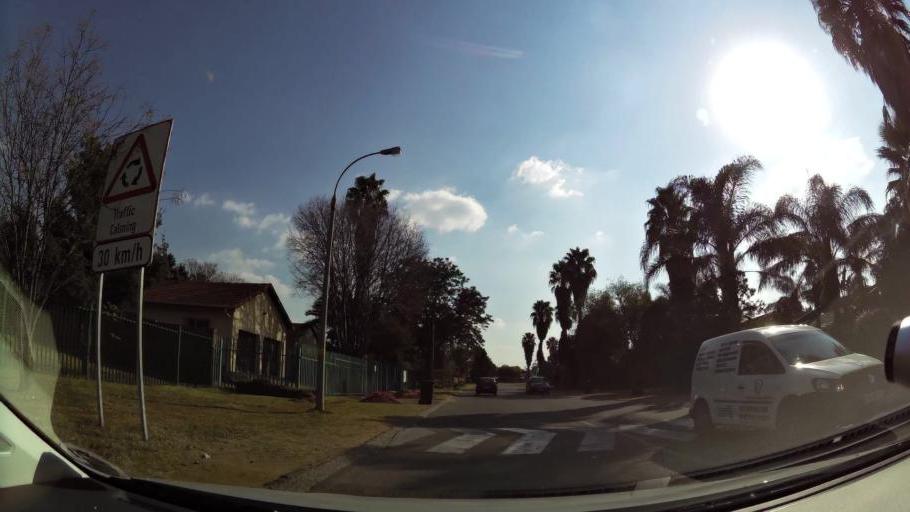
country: ZA
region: Gauteng
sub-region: City of Johannesburg Metropolitan Municipality
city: Modderfontein
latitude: -26.0903
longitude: 28.2017
